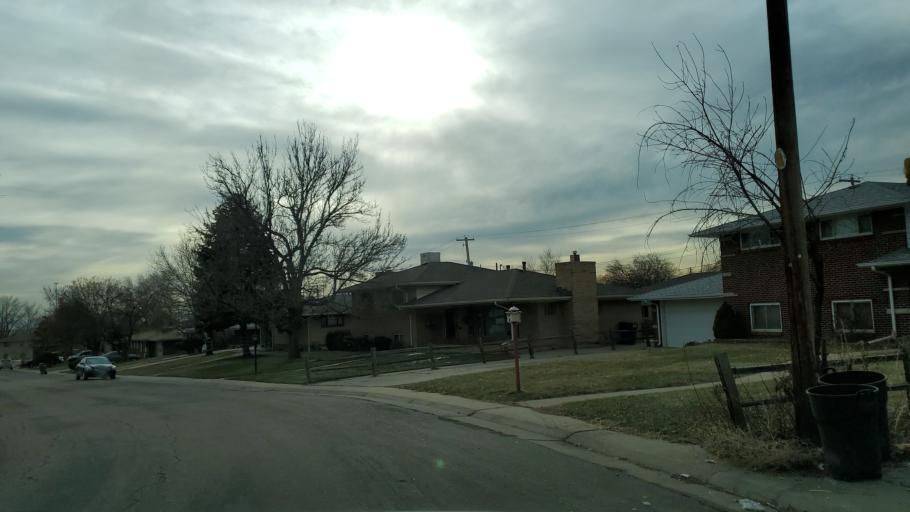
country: US
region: Colorado
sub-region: Adams County
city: Westminster
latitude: 39.8409
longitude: -105.0234
